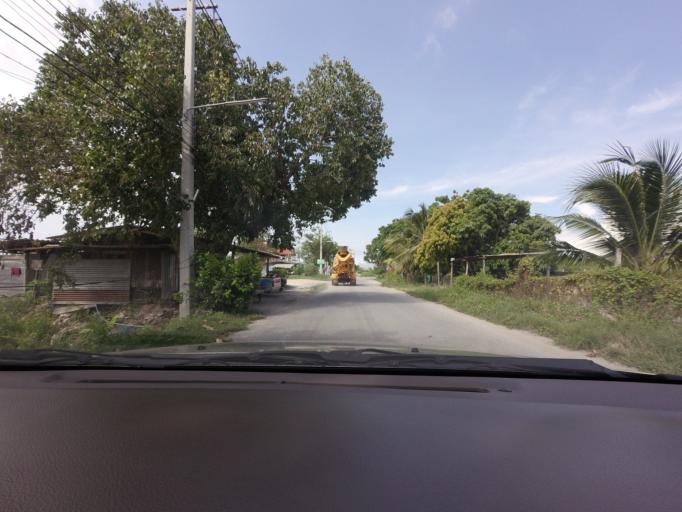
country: TH
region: Chon Buri
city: Chon Buri
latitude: 13.3191
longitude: 100.9995
